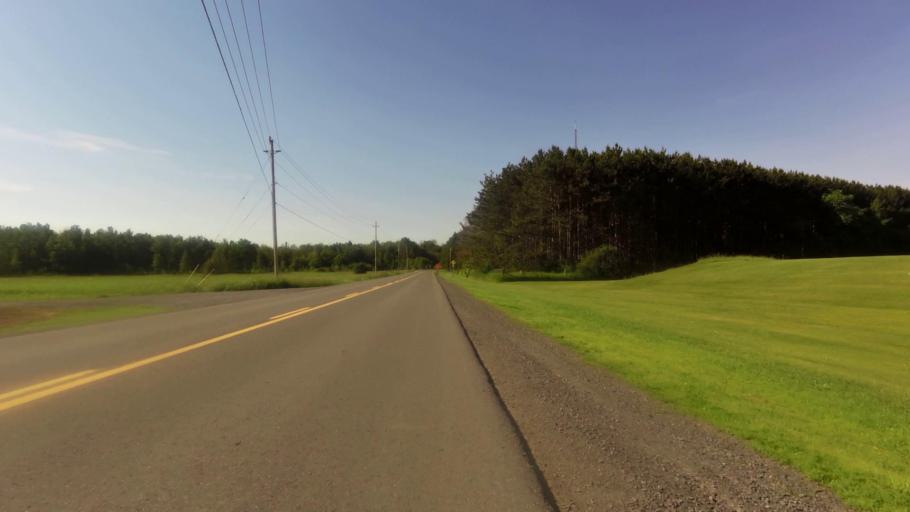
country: CA
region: Ontario
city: Ottawa
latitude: 45.2245
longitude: -75.5609
